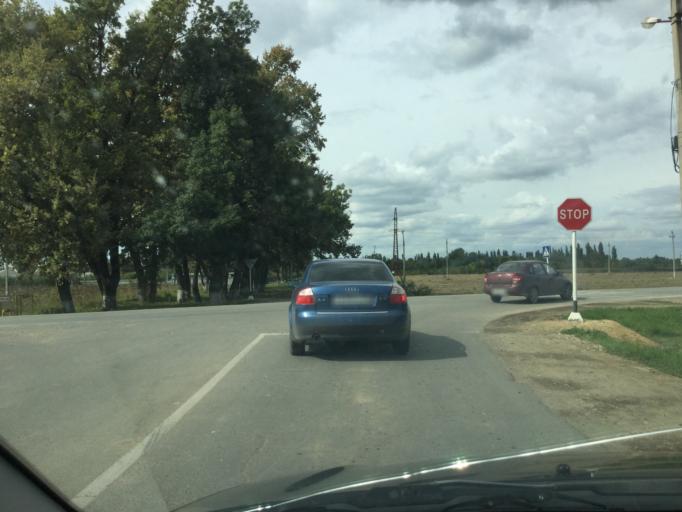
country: RU
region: Krasnodarskiy
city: Sovkhoznyy
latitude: 45.2757
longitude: 38.0951
